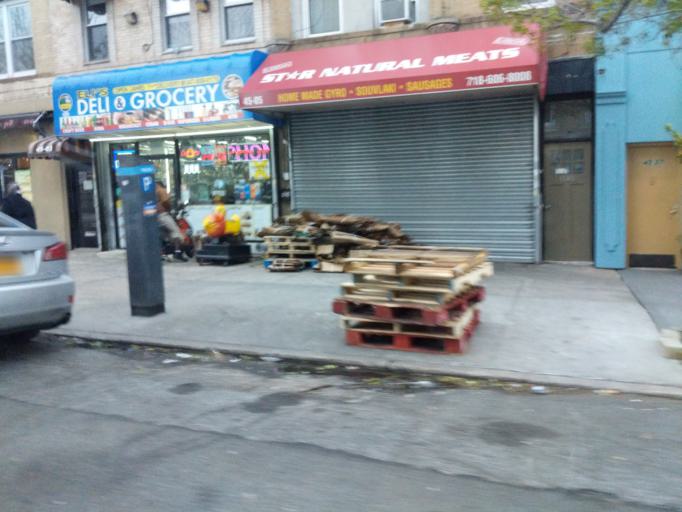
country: US
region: New York
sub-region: Queens County
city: Long Island City
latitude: 40.7707
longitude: -73.9029
